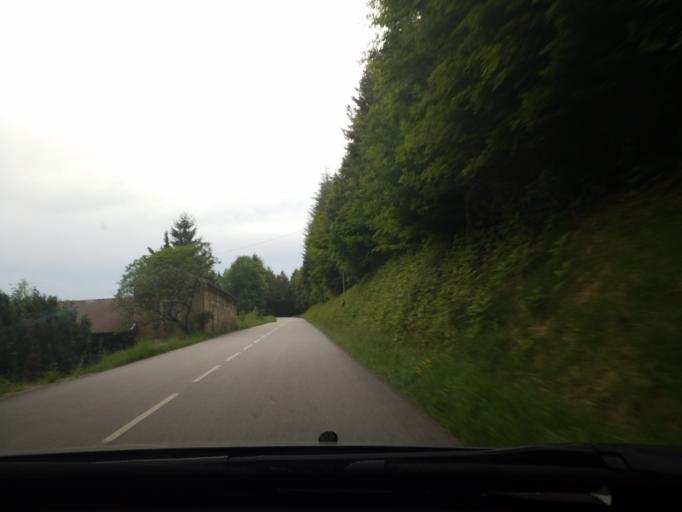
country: FR
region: Lorraine
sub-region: Departement des Vosges
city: Bains-les-Bains
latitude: 48.0308
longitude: 6.1980
